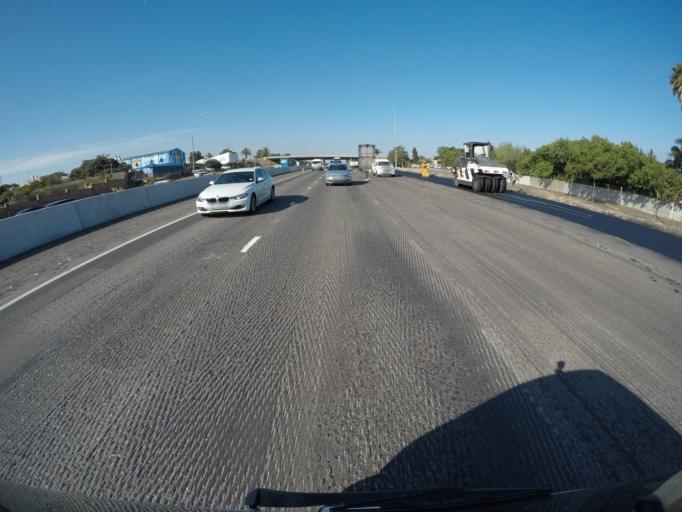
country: ZA
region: Western Cape
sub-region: City of Cape Town
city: Kraaifontein
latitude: -33.8832
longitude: 18.6444
